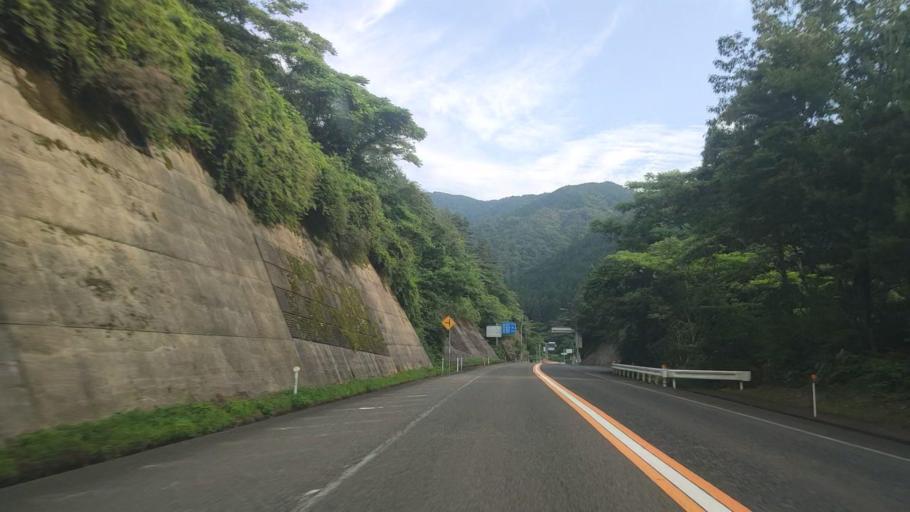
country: JP
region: Tottori
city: Kurayoshi
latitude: 35.3207
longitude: 133.7564
